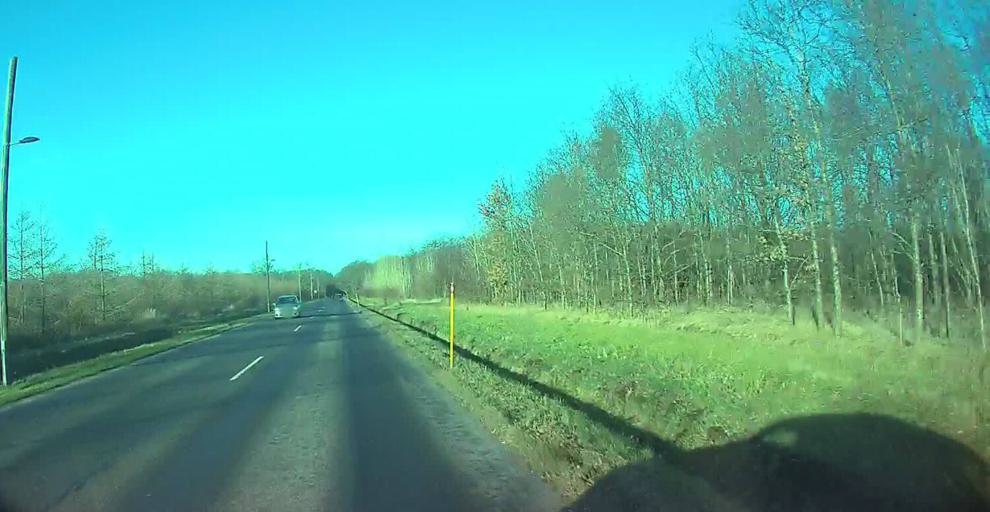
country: DK
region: Capital Region
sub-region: Tarnby Kommune
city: Tarnby
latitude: 55.5692
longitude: 12.5833
